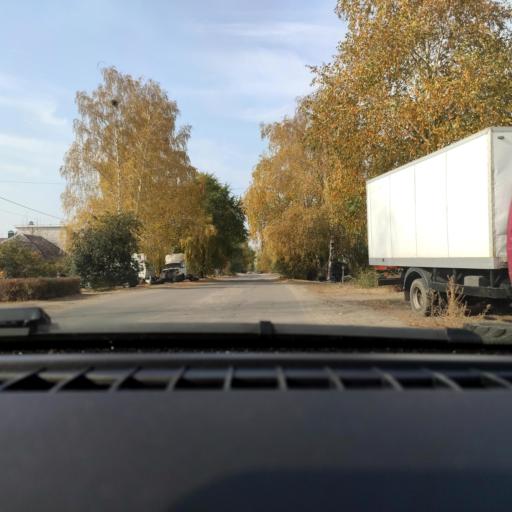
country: RU
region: Voronezj
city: Maslovka
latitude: 51.6293
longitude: 39.2748
